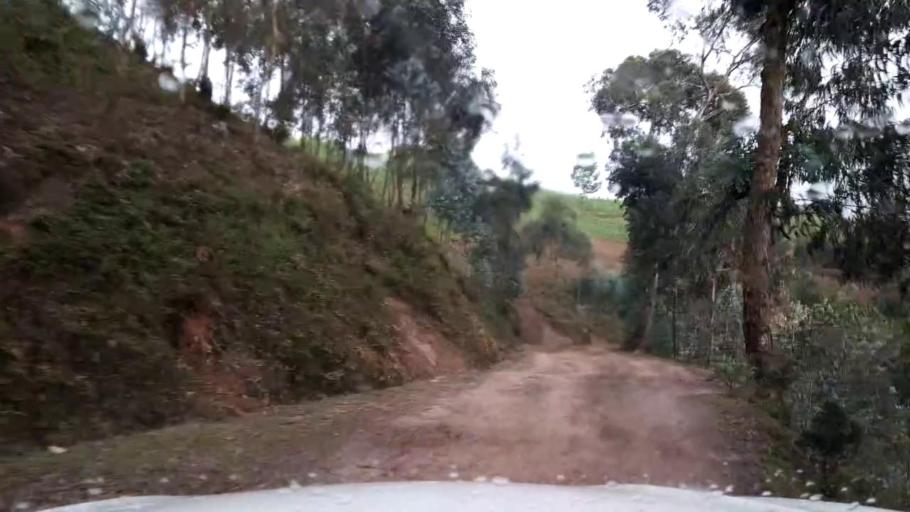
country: RW
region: Western Province
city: Kibuye
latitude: -1.9715
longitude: 29.4865
